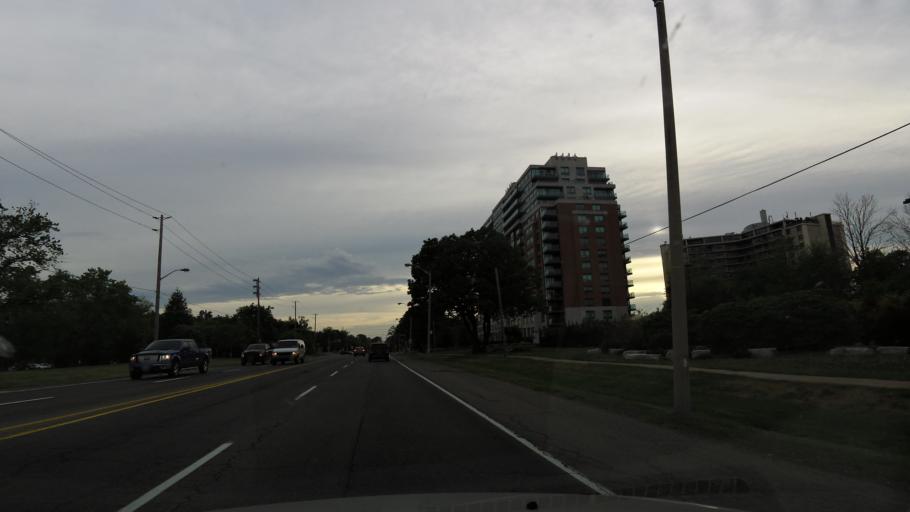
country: CA
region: Ontario
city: Etobicoke
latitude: 43.6830
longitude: -79.5244
